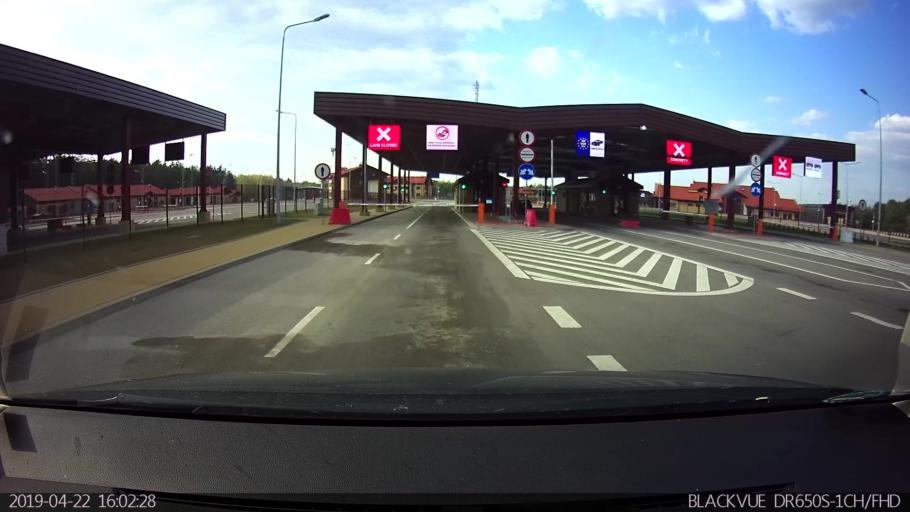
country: PL
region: Podlasie
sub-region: Powiat hajnowski
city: Czeremcha
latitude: 52.4748
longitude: 23.3573
